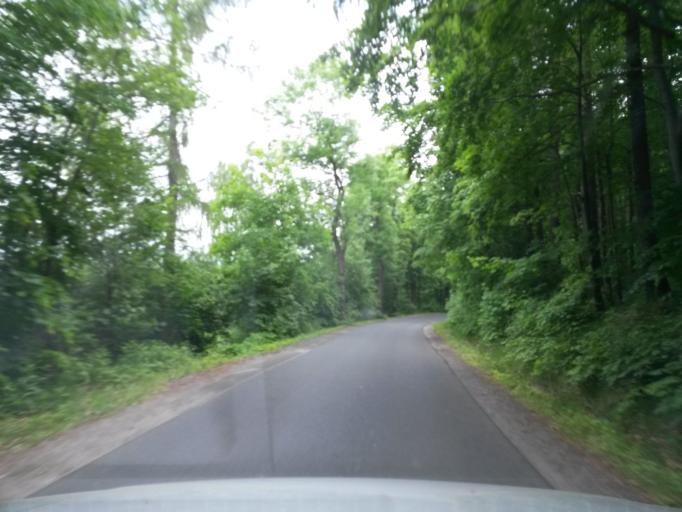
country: PL
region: Lower Silesian Voivodeship
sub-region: Powiat jeleniogorski
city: Podgorzyn
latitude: 50.8328
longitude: 15.6626
